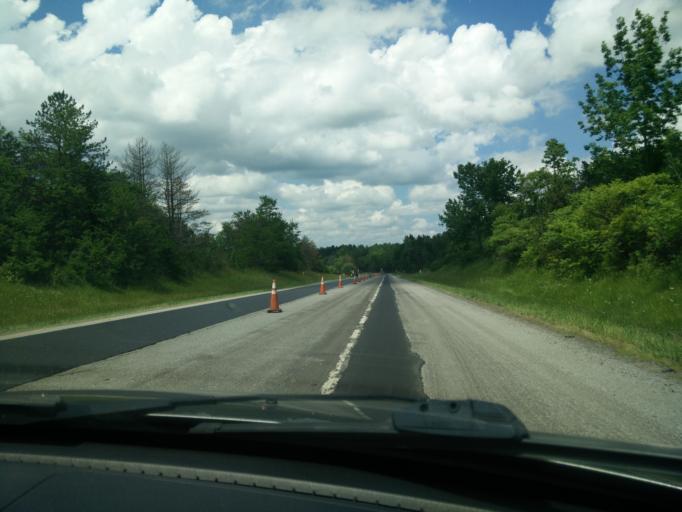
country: US
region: New York
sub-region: Erie County
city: East Aurora
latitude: 42.7871
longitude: -78.5964
